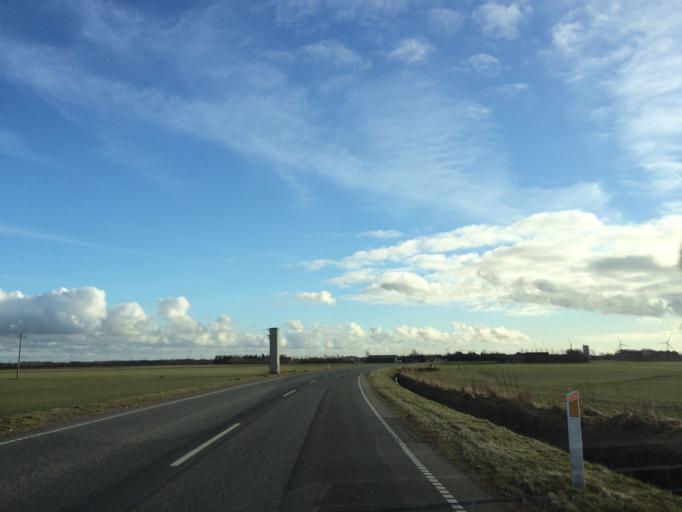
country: DK
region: Central Jutland
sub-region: Lemvig Kommune
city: Lemvig
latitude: 56.4281
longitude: 8.3038
